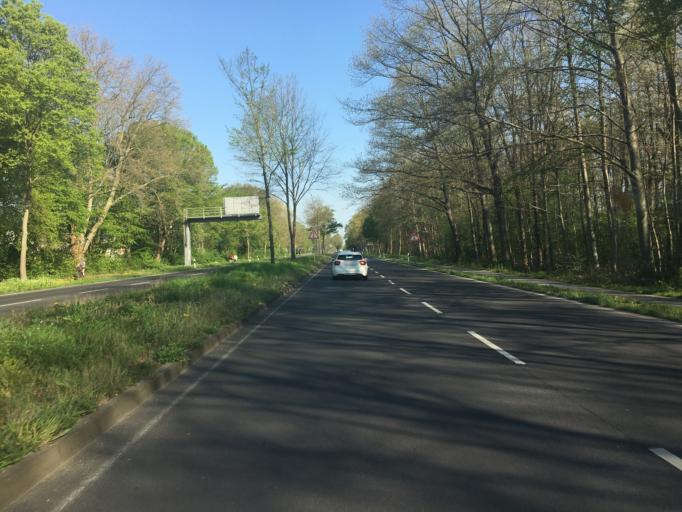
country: DE
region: North Rhine-Westphalia
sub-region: Regierungsbezirk Koln
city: Muelheim
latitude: 50.9956
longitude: 6.9977
